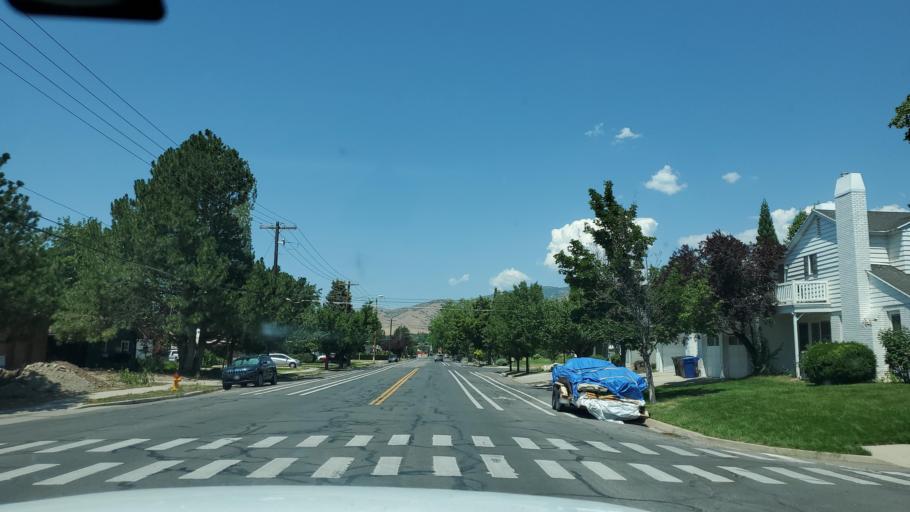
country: US
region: Utah
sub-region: Salt Lake County
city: Canyon Rim
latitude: 40.7211
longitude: -111.8245
